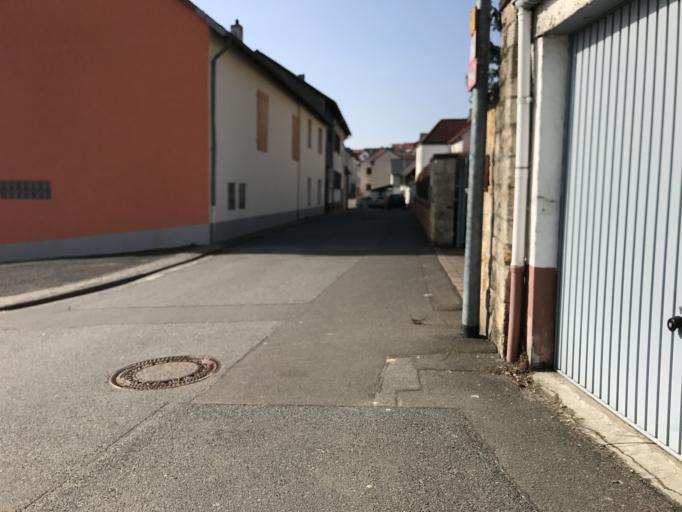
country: DE
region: Rheinland-Pfalz
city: Essenheim
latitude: 49.9302
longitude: 8.1546
